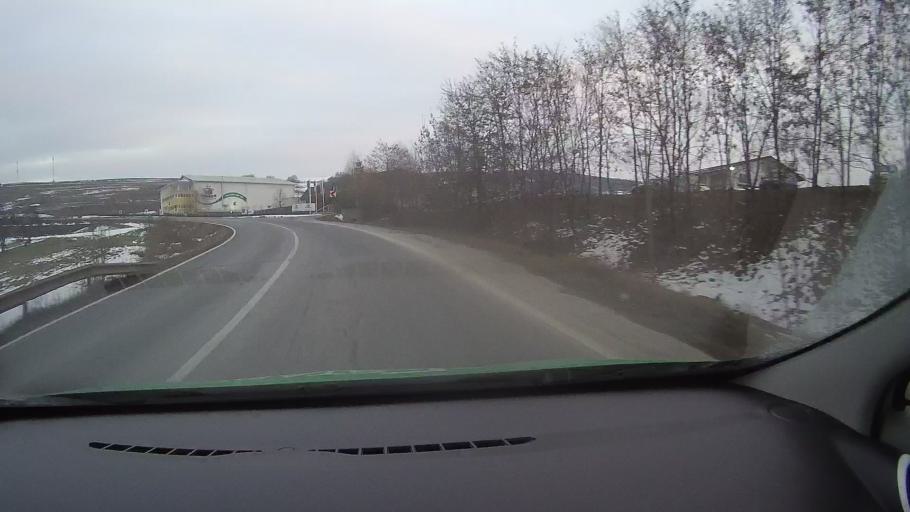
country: RO
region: Harghita
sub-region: Comuna Lupeni
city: Lupeni
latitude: 46.3559
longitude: 25.2396
